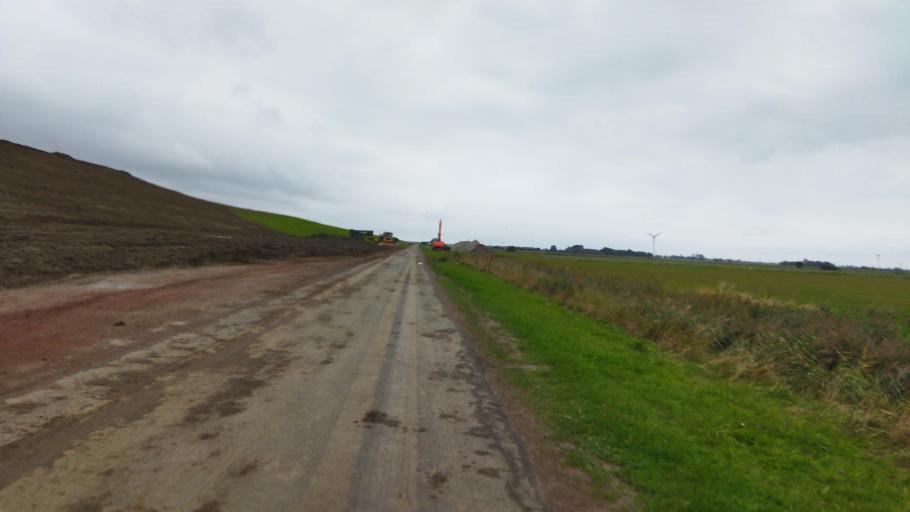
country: NL
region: Groningen
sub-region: Gemeente Delfzijl
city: Delfzijl
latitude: 53.4439
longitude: 7.0206
